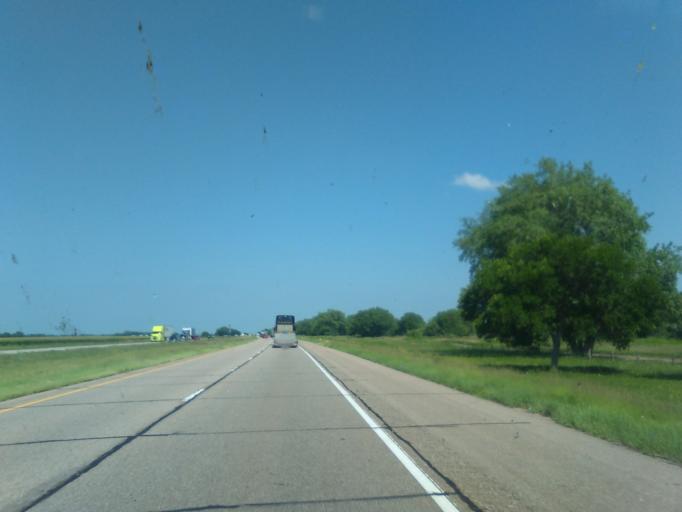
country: US
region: Nebraska
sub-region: Buffalo County
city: Kearney
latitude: 40.6722
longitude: -99.2169
